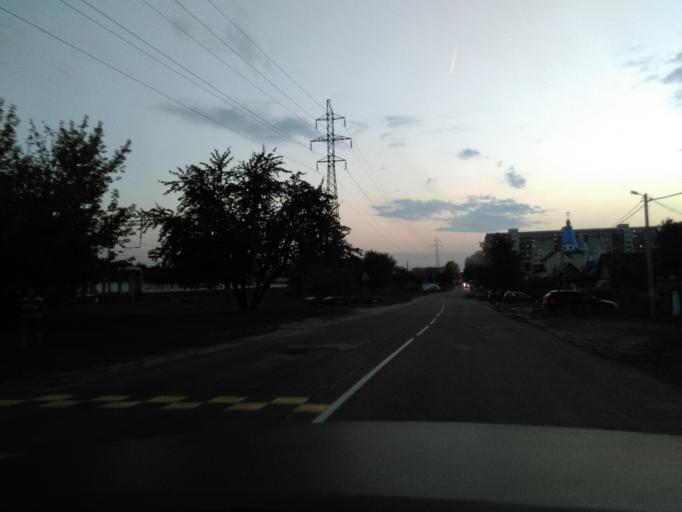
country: BY
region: Minsk
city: Minsk
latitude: 53.9015
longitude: 27.6280
